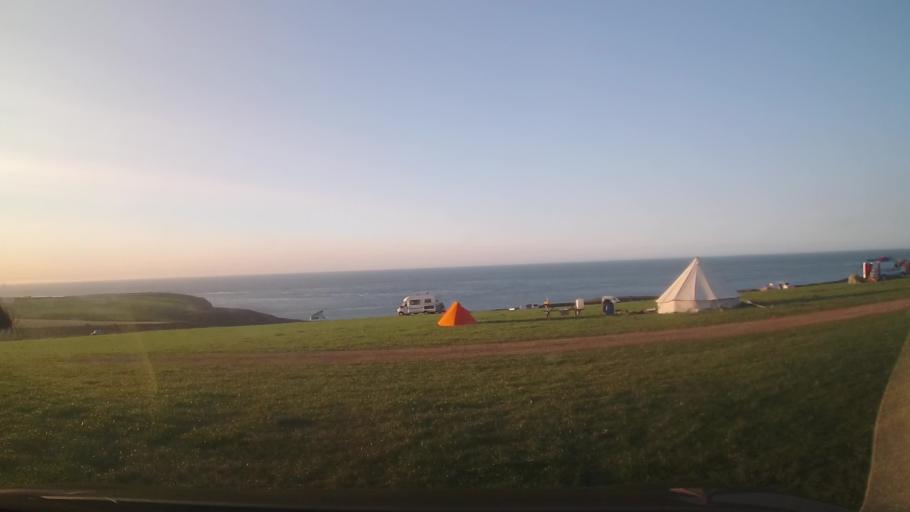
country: GB
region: Wales
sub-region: Pembrokeshire
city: Llanrhian
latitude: 51.9262
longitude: -5.2215
